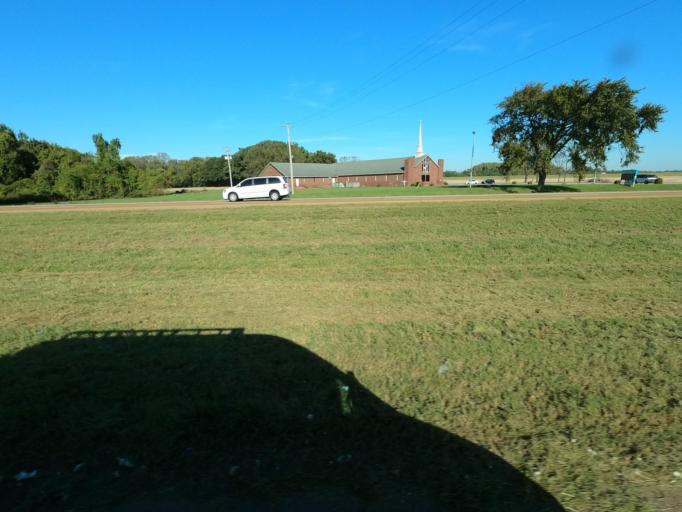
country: US
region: Tennessee
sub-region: Shelby County
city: Millington
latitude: 35.3691
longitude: -89.8841
